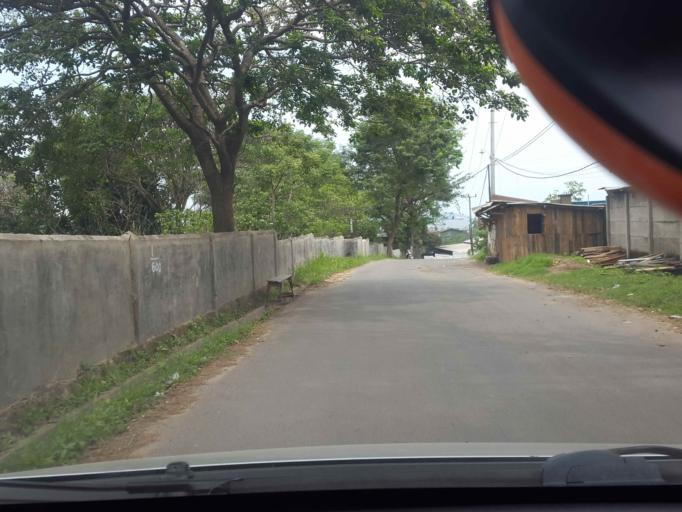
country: ID
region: Lampung
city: Panjang
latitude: -5.4393
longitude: 105.2999
